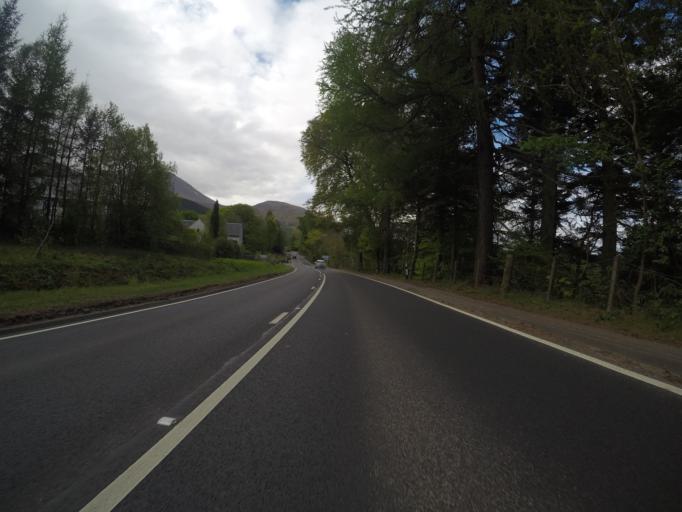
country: GB
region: Scotland
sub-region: Highland
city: Fort William
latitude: 56.8485
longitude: -5.0463
